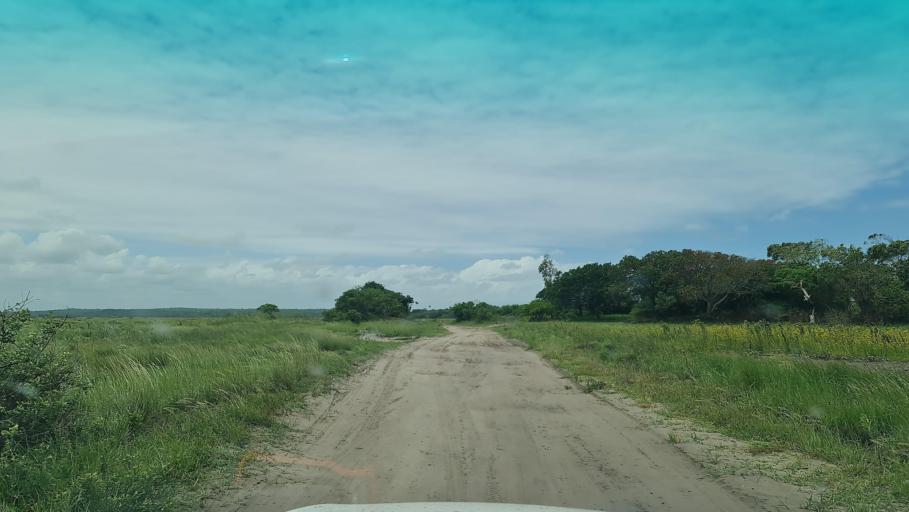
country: MZ
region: Maputo
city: Manhica
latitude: -25.5270
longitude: 32.8532
